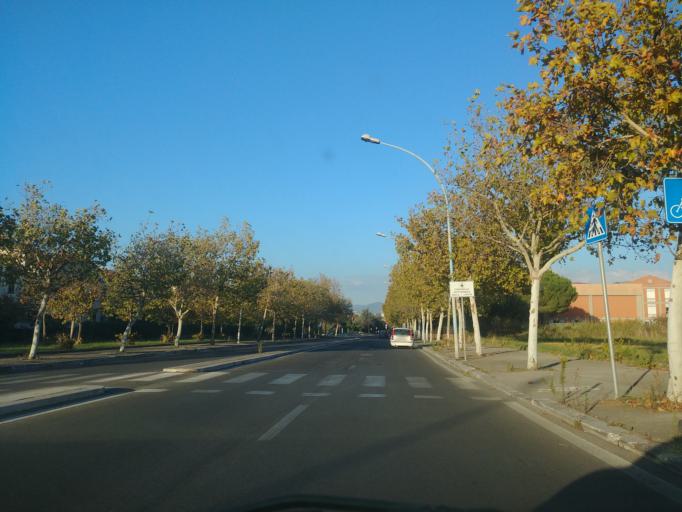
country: IT
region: Latium
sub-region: Provincia di Latina
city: Latina
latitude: 41.4545
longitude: 12.9009
